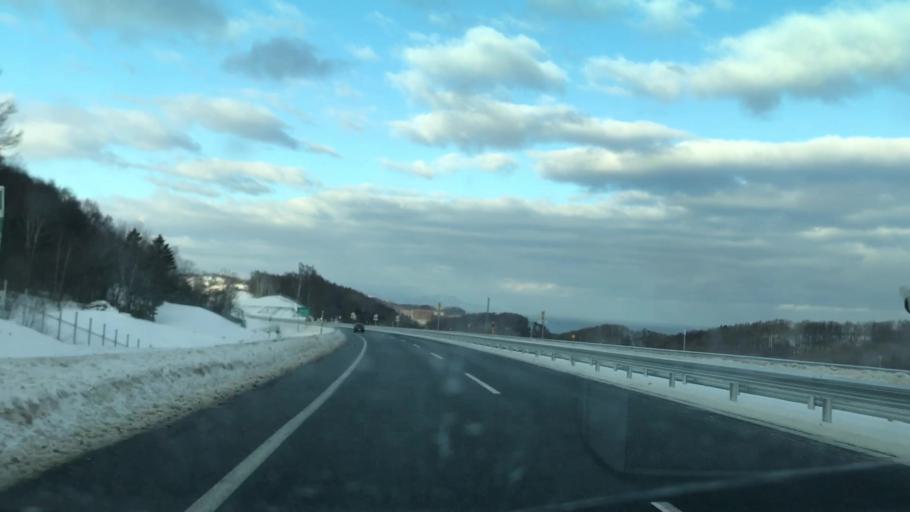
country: JP
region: Hokkaido
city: Otaru
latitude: 43.1993
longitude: 140.9440
